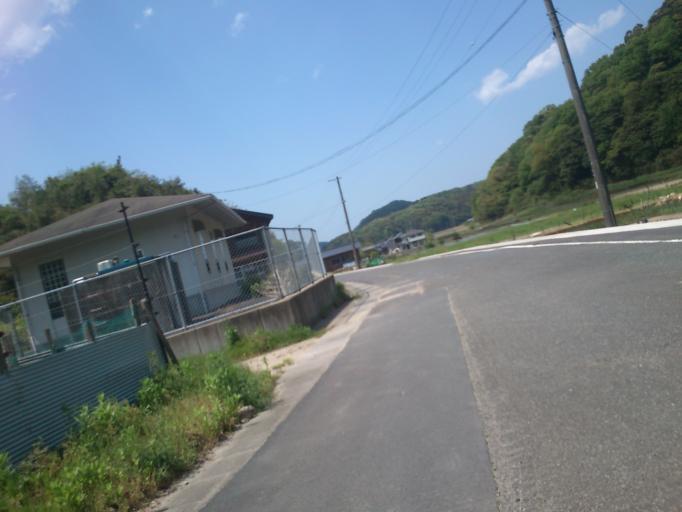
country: JP
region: Kyoto
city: Miyazu
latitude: 35.7076
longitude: 135.1184
